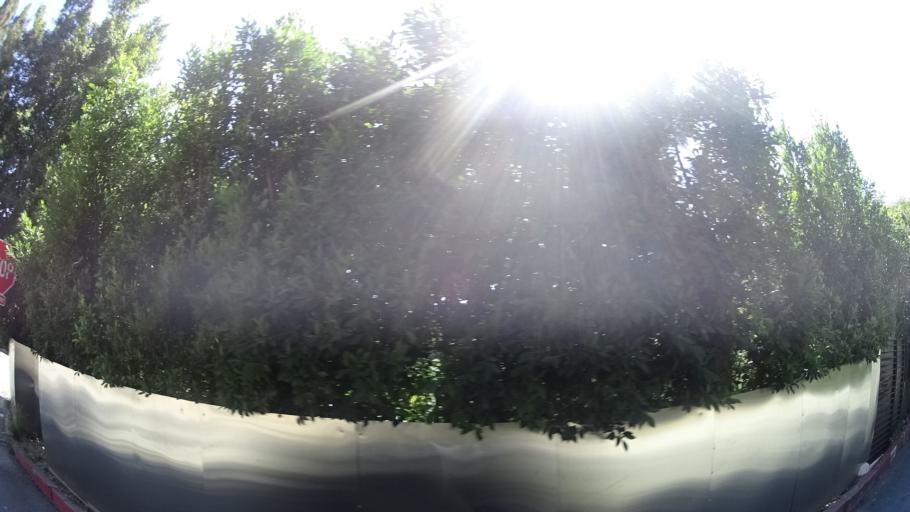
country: US
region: California
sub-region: Los Angeles County
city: West Hollywood
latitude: 34.1003
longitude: -118.3806
